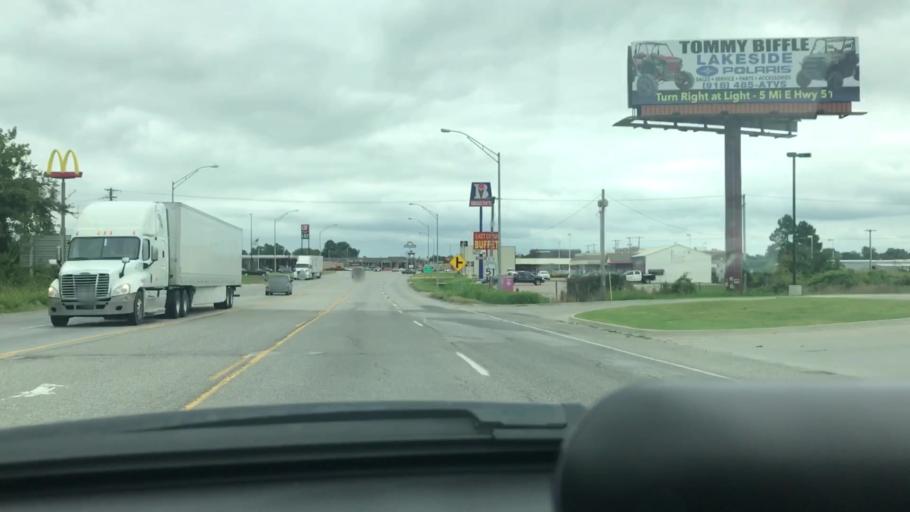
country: US
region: Oklahoma
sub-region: Wagoner County
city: Wagoner
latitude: 35.9556
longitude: -95.3952
